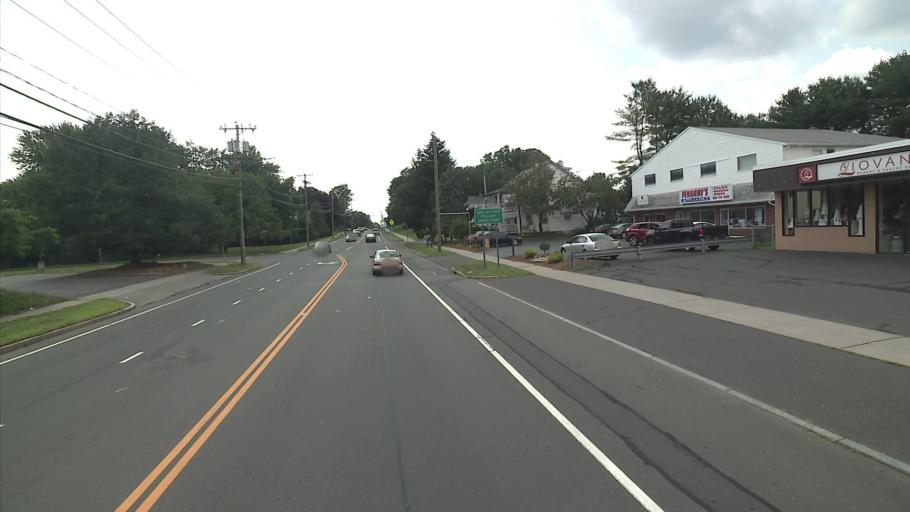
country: US
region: Connecticut
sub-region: Hartford County
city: Newington
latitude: 41.6738
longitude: -72.7414
